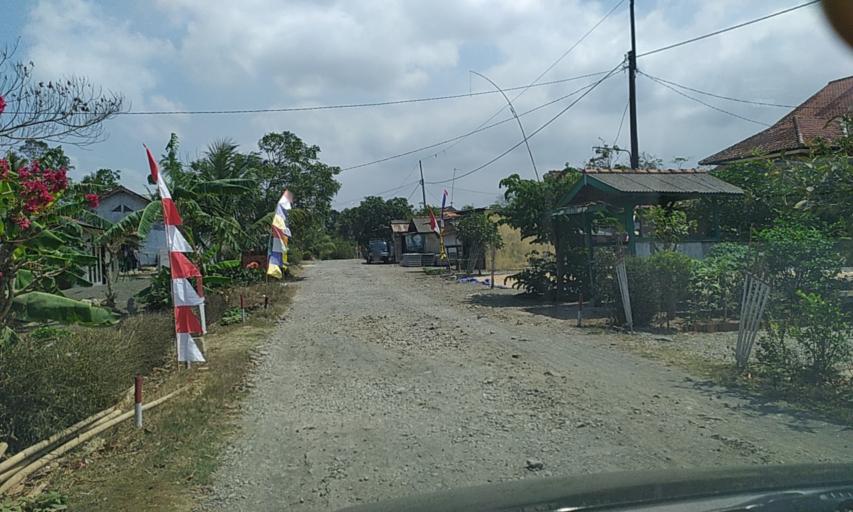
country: ID
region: Central Java
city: Madusari
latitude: -7.6380
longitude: 109.0706
